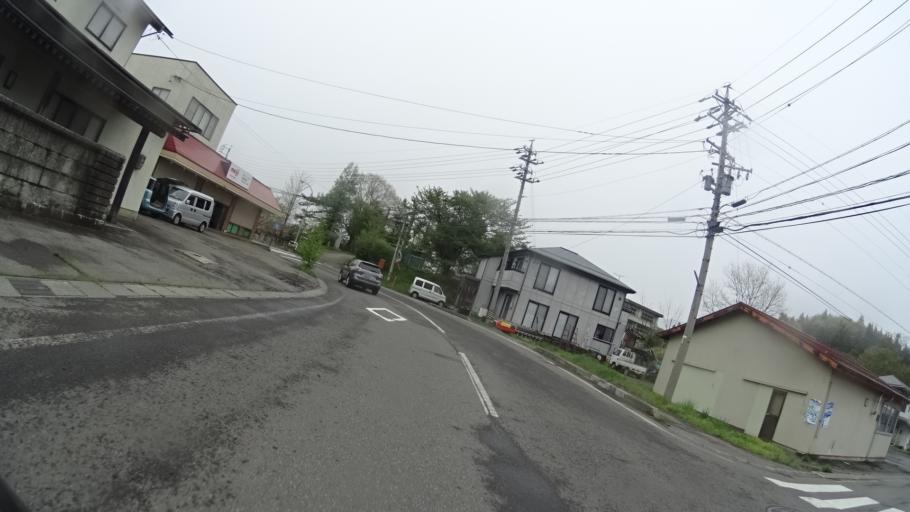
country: JP
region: Nagano
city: Nagano-shi
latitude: 36.7745
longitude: 138.2023
